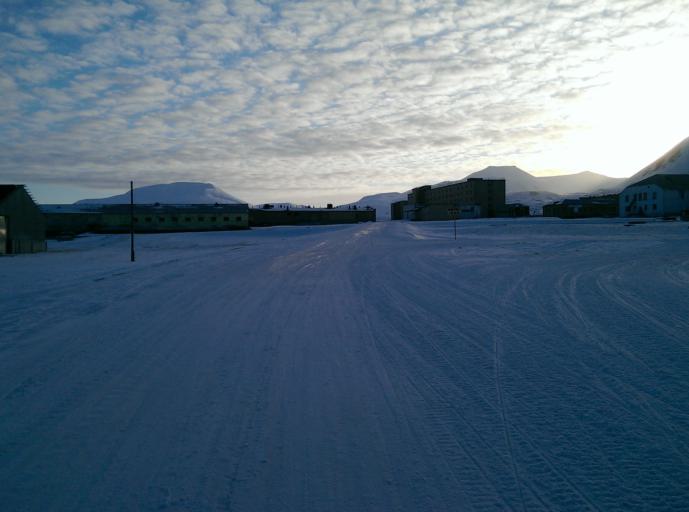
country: SJ
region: Svalbard
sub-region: Spitsbergen
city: Longyearbyen
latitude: 78.6535
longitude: 16.3323
